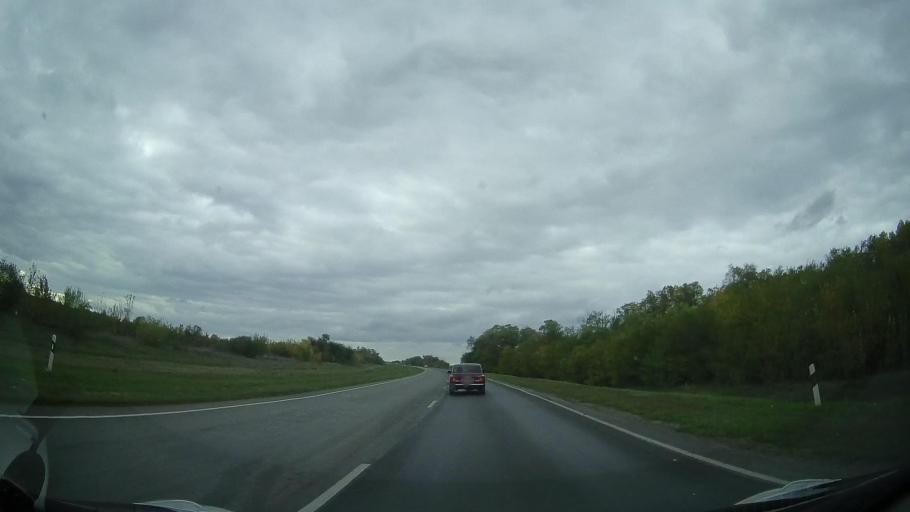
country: RU
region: Rostov
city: Yegorlykskaya
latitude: 46.5455
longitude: 40.7646
